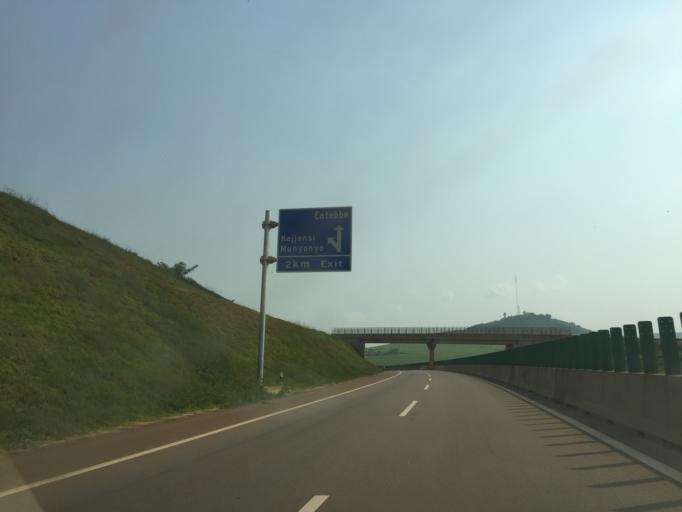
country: UG
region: Central Region
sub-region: Wakiso District
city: Kajansi
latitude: 0.2338
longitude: 32.5235
